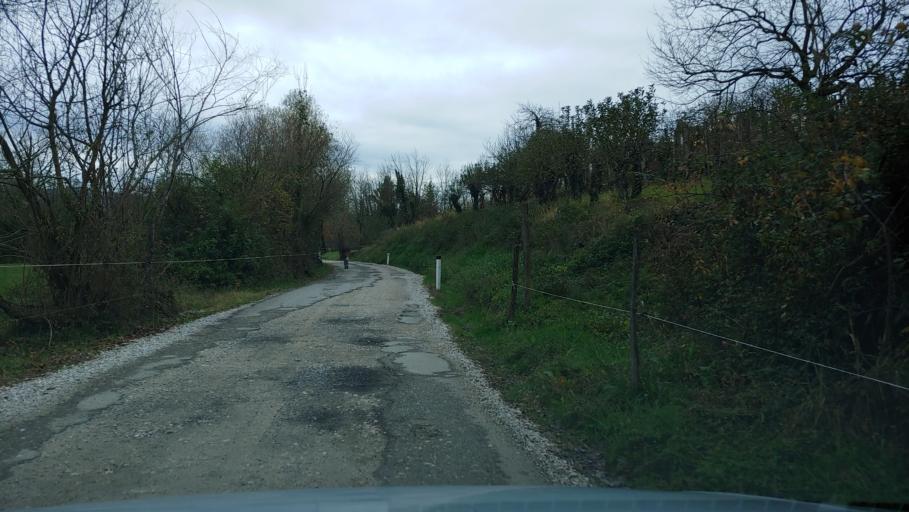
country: SI
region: Sempeter-Vrtojba
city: Sempeter pri Gorici
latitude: 45.9175
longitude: 13.6466
